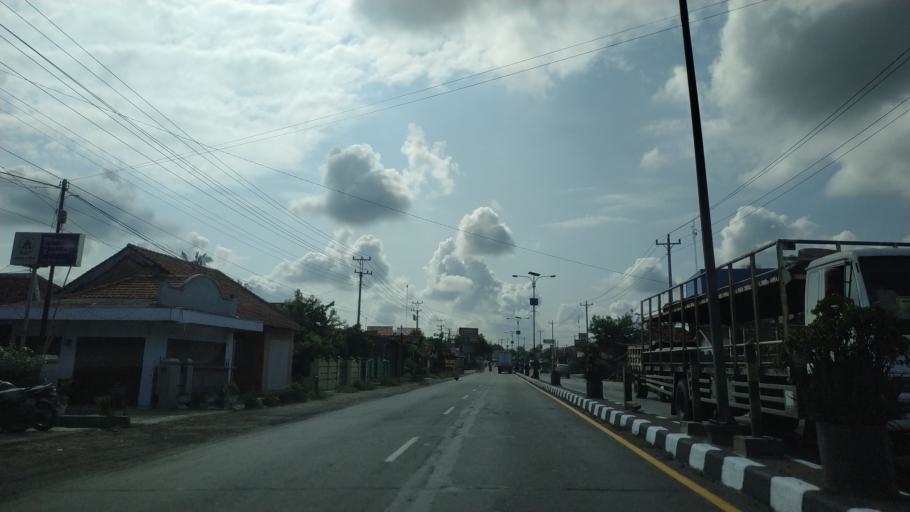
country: ID
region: Central Java
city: Comal
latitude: -6.9002
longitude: 109.5209
